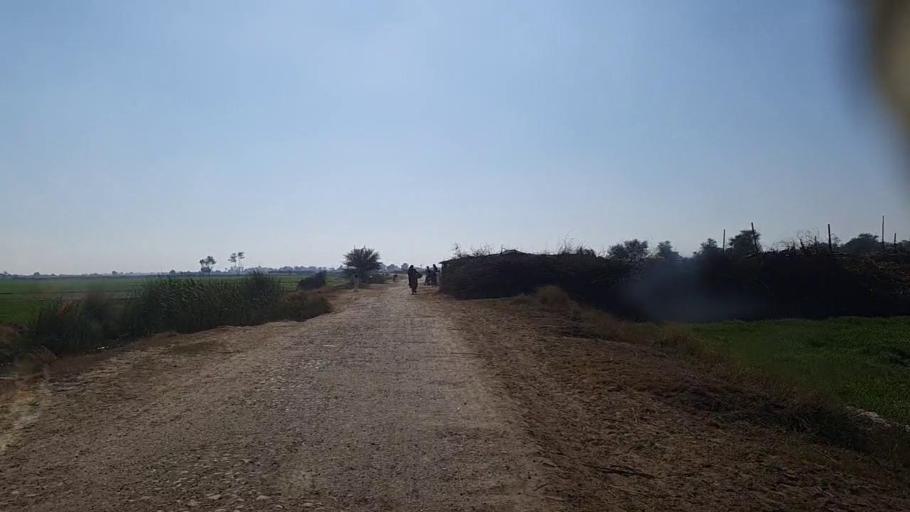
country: PK
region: Sindh
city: Khairpur
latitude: 28.0385
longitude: 69.7826
